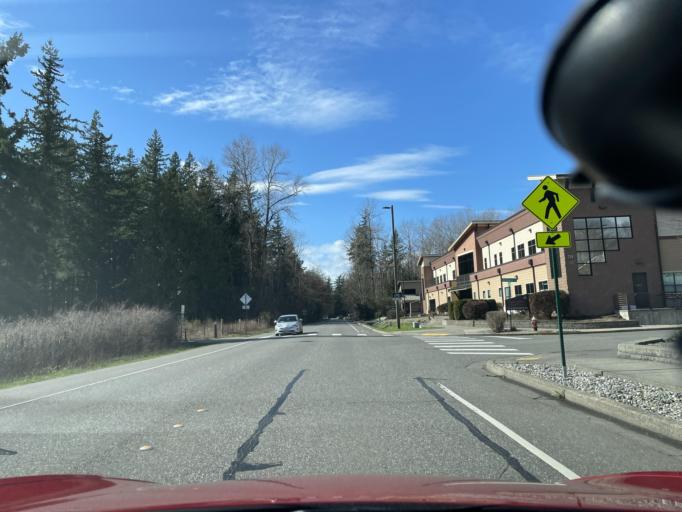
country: US
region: Washington
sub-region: Whatcom County
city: Bellingham
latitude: 48.7772
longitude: -122.4802
